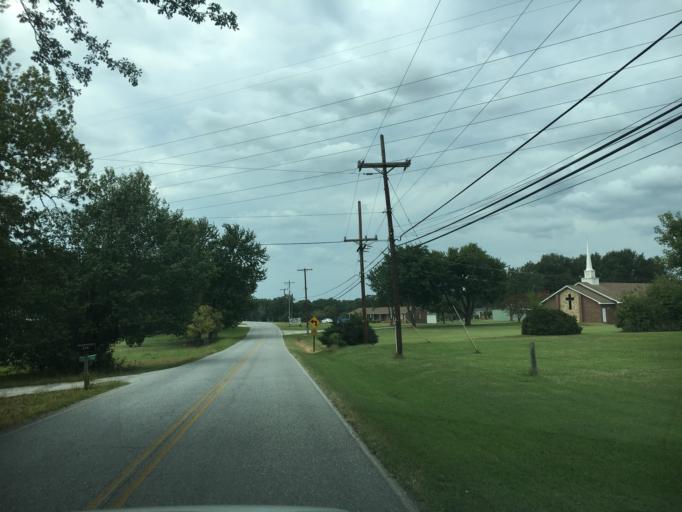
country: US
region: South Carolina
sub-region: Greenville County
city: Greer
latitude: 34.9269
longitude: -82.2059
